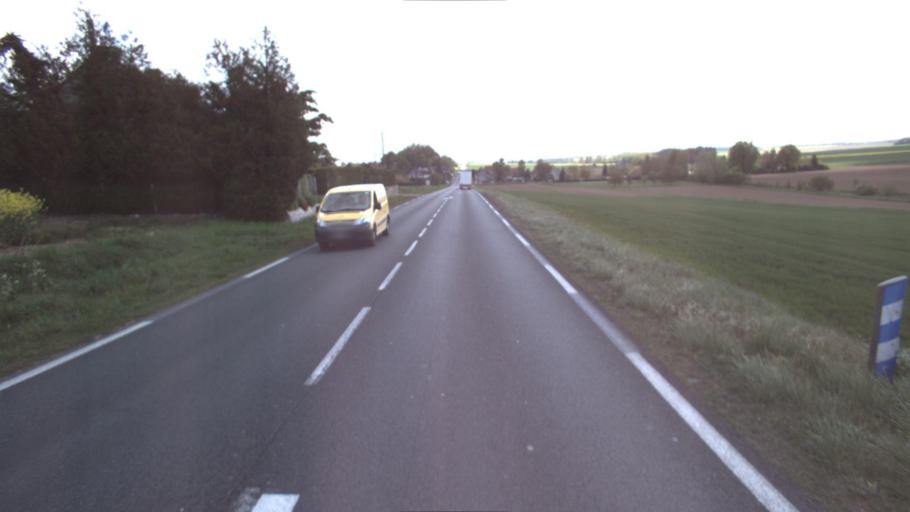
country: FR
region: Ile-de-France
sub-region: Departement de Seine-et-Marne
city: Choisy-en-Brie
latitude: 48.6999
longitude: 3.2629
